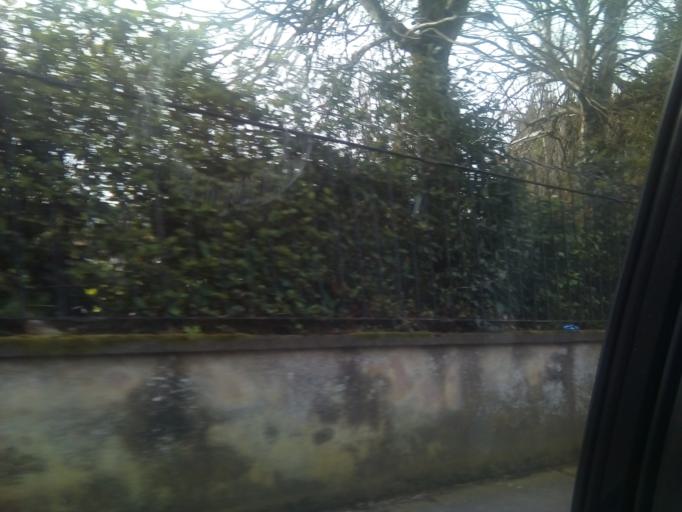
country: IE
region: Munster
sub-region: County Cork
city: Cork
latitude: 51.8921
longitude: -8.4900
